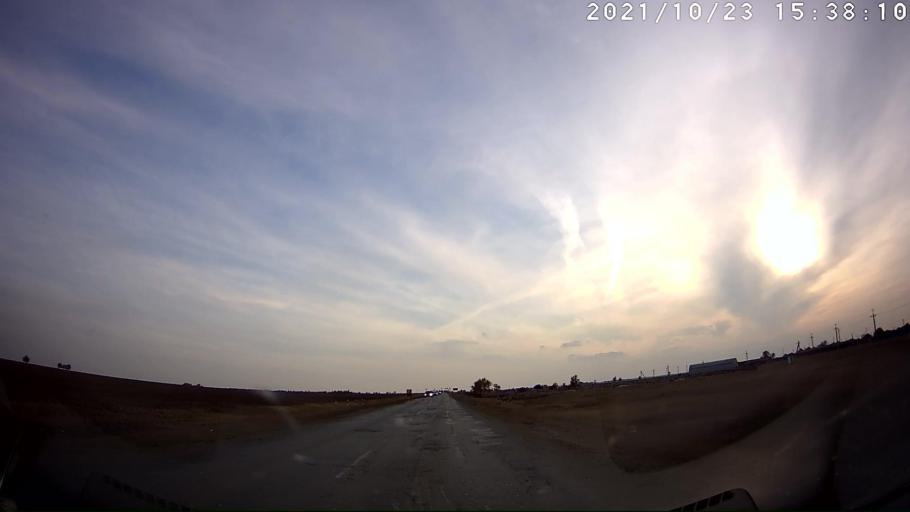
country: RU
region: Volgograd
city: Bereslavka
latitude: 48.1368
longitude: 44.1209
